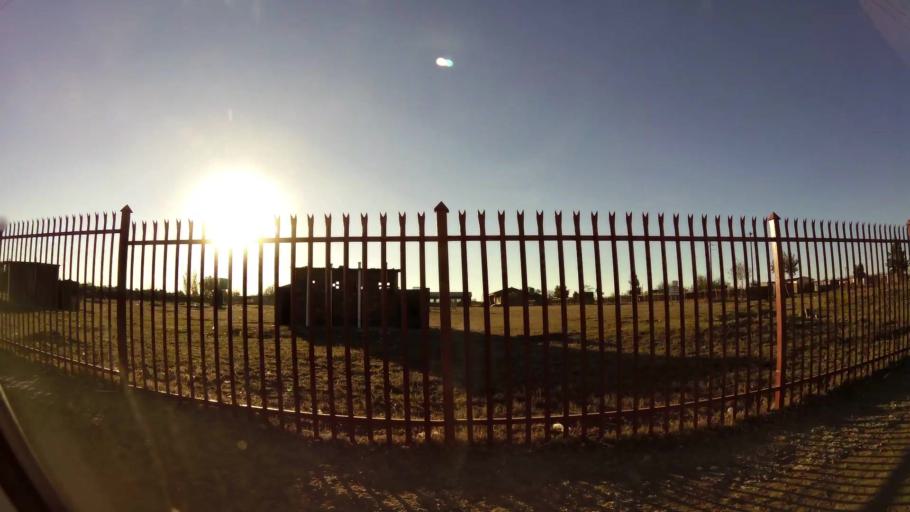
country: ZA
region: Limpopo
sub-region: Capricorn District Municipality
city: Polokwane
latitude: -23.8178
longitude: 29.3821
